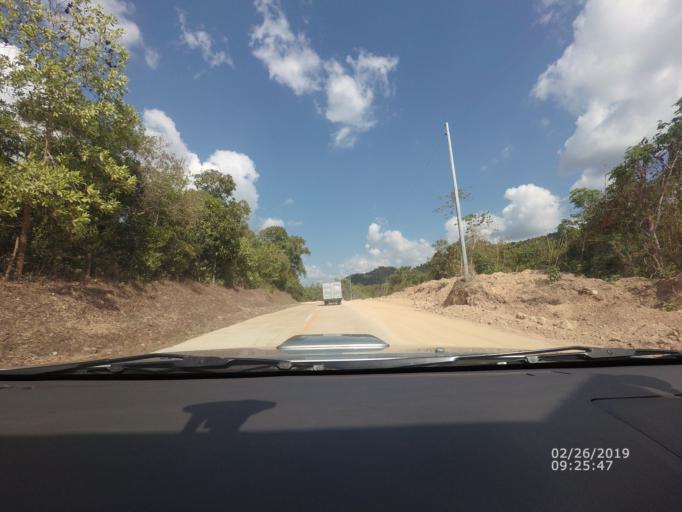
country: PH
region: Mimaropa
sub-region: Province of Palawan
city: Salvacion
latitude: 12.0349
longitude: 120.0382
